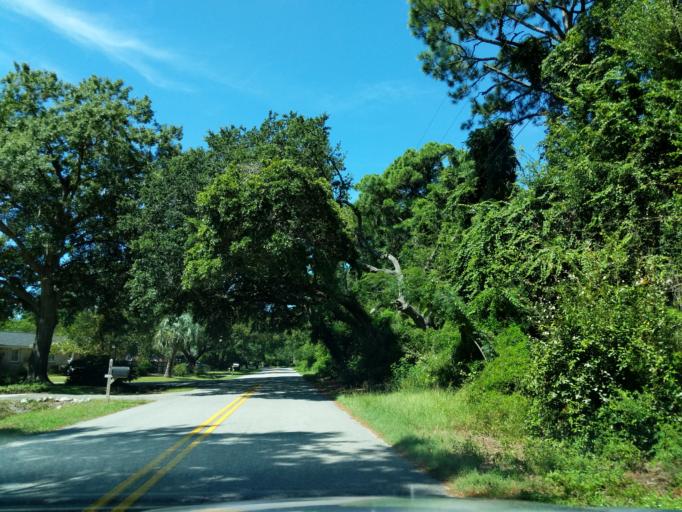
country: US
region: South Carolina
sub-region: Charleston County
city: Folly Beach
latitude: 32.7041
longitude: -79.9483
